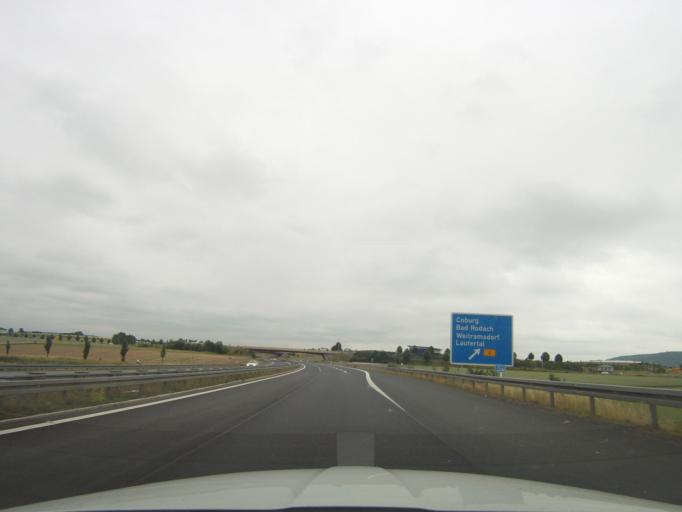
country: DE
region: Bavaria
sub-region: Upper Franconia
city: Coburg
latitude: 50.2911
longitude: 10.9743
